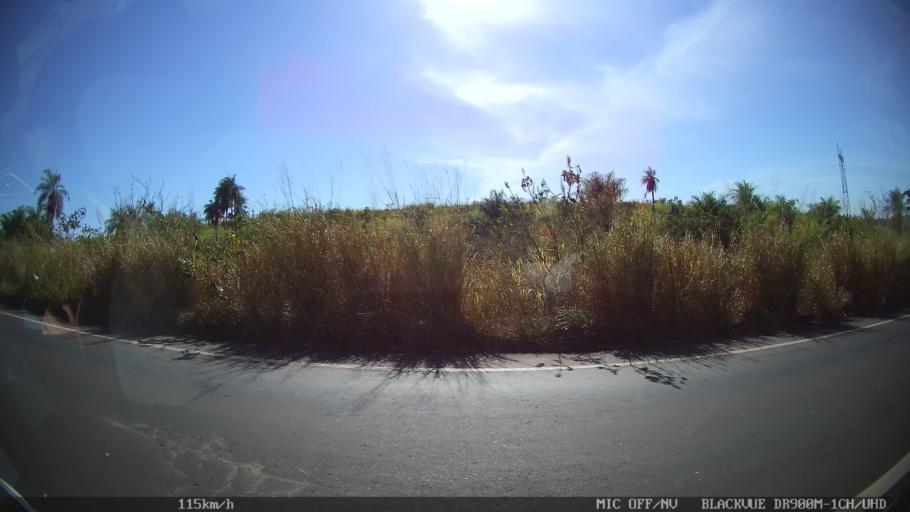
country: BR
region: Sao Paulo
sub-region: Olimpia
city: Olimpia
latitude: -20.6333
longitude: -48.8154
